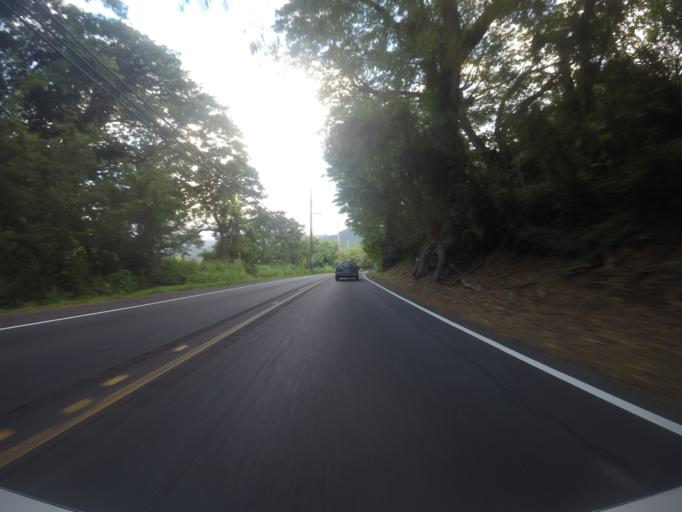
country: US
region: Hawaii
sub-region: Honolulu County
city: Ka'a'awa
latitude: 21.5157
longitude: -157.8416
